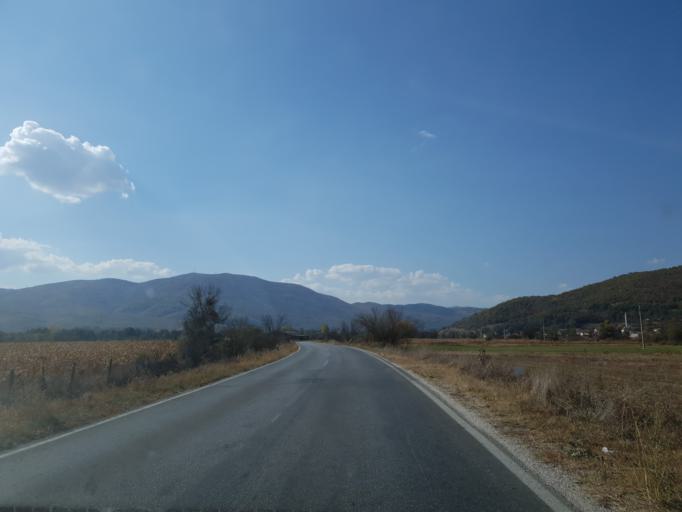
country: MK
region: Plasnica
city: Lisicani
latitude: 41.4702
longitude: 21.0402
